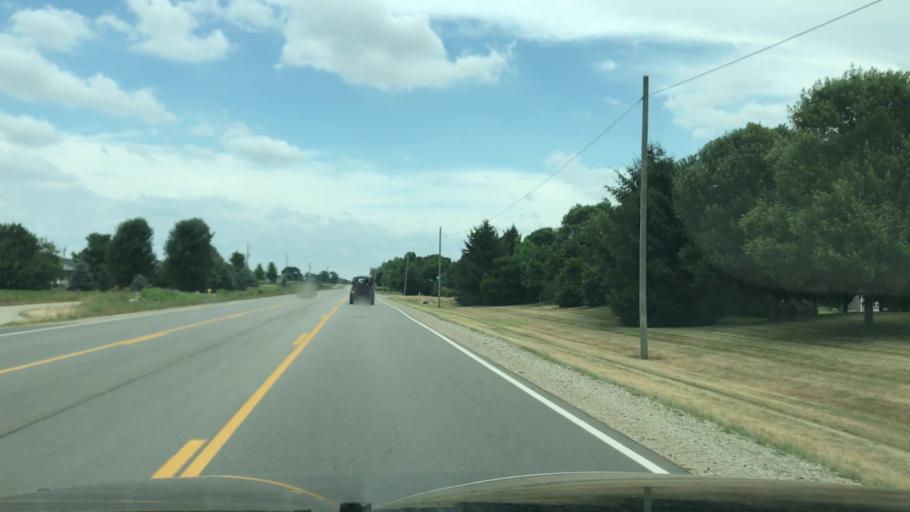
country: US
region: Michigan
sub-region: Ottawa County
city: Zeeland
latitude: 42.7833
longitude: -85.9744
